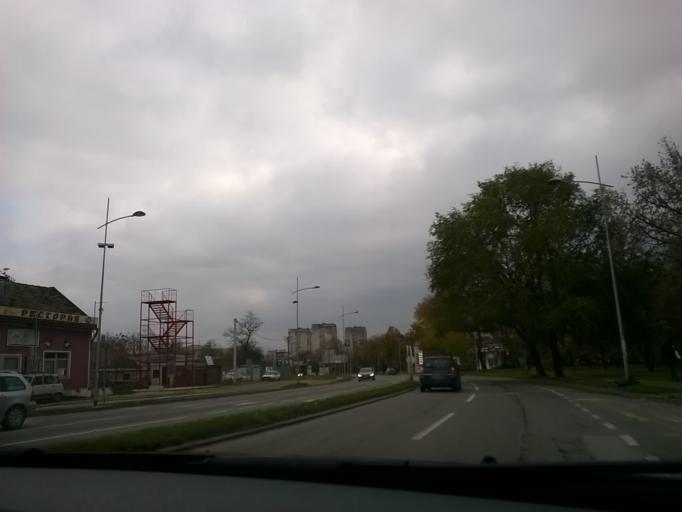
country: RS
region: Autonomna Pokrajina Vojvodina
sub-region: Juznobacki Okrug
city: Novi Sad
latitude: 45.2689
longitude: 19.8317
